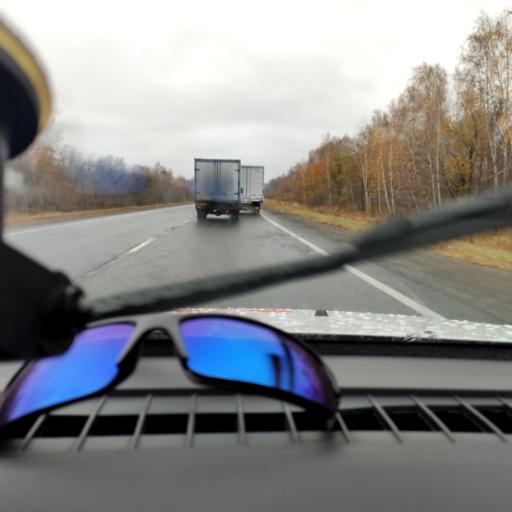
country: RU
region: Samara
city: Chapayevsk
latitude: 52.9916
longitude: 49.8392
